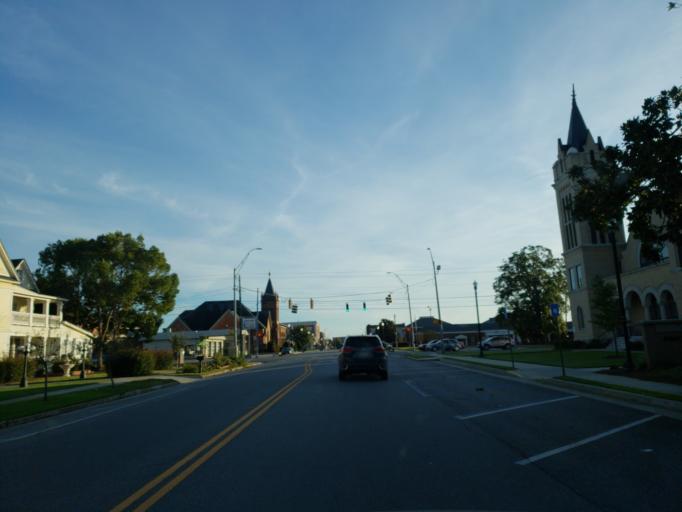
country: US
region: Georgia
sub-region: Tift County
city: Tifton
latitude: 31.4567
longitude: -83.5083
